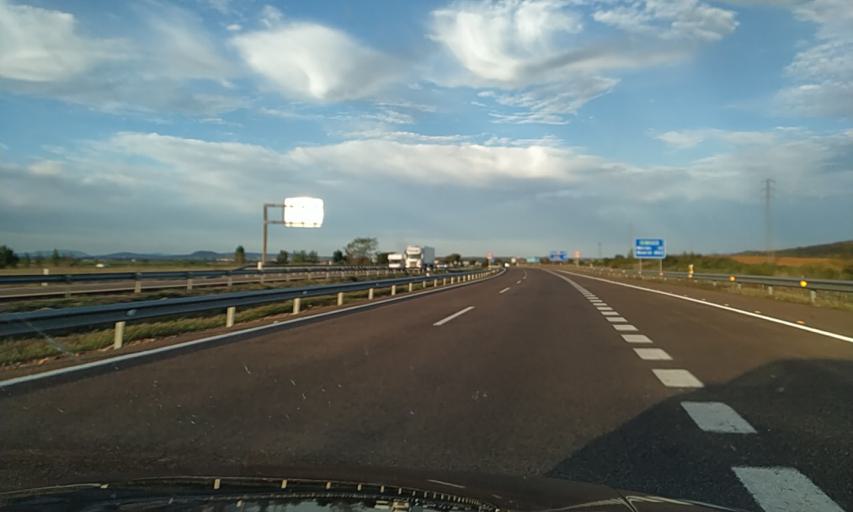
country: ES
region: Extremadura
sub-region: Provincia de Badajoz
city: Arroyo de San Servan
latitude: 38.8746
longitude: -6.4710
